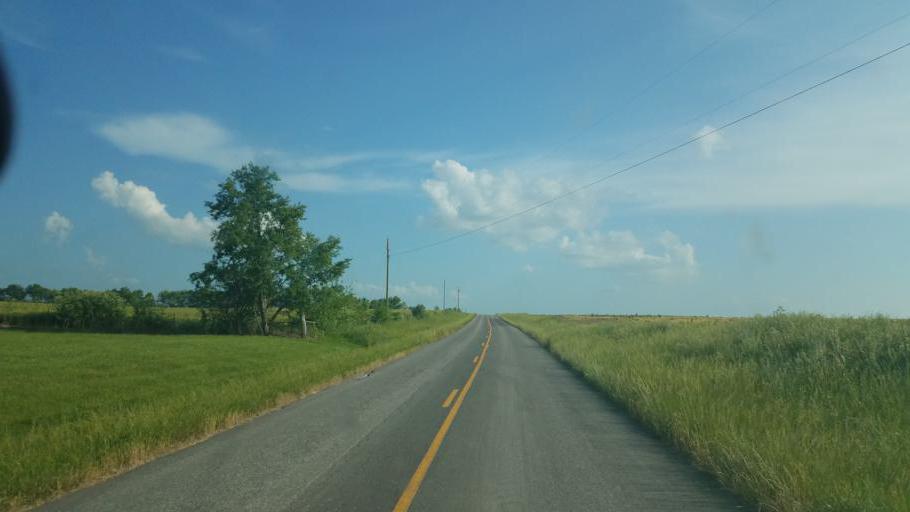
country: US
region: Missouri
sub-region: Moniteau County
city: California
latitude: 38.7970
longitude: -92.6050
